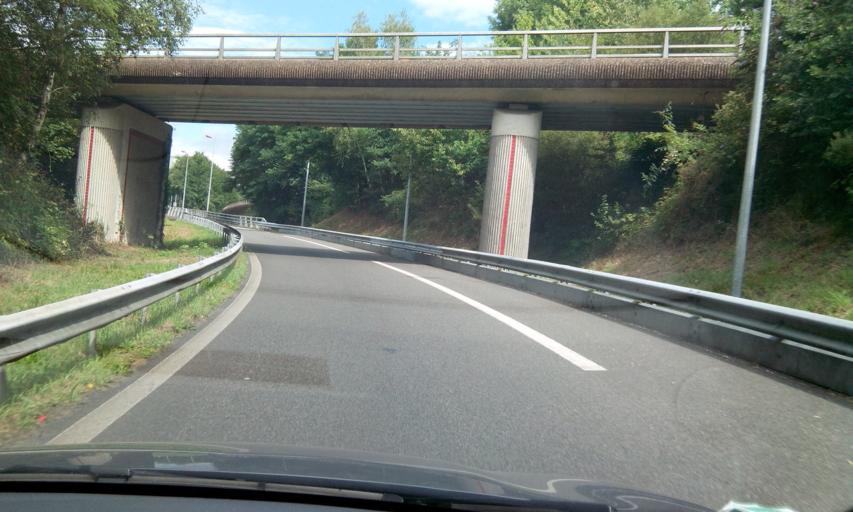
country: FR
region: Limousin
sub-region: Departement de la Haute-Vienne
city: Limoges
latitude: 45.8488
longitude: 1.2771
